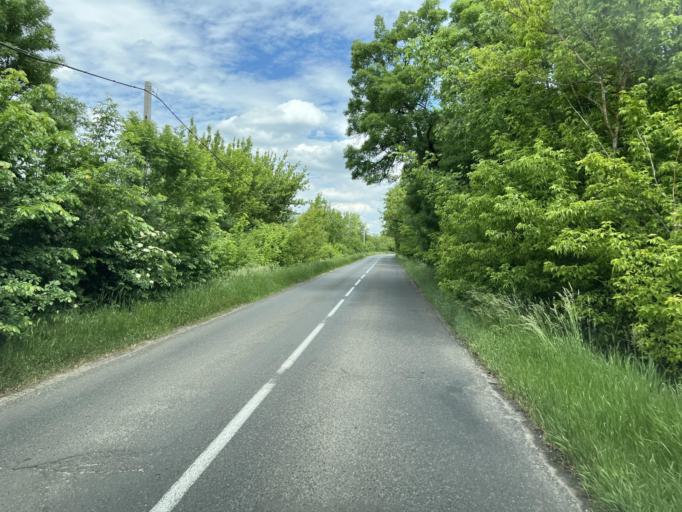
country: HU
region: Pest
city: Toalmas
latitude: 47.4941
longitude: 19.6487
